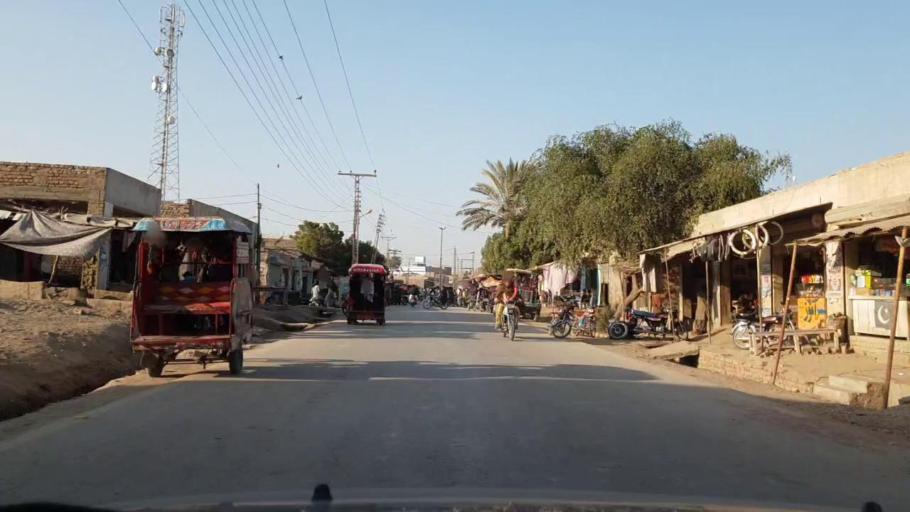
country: PK
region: Sindh
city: Chambar
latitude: 25.2908
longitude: 68.8114
